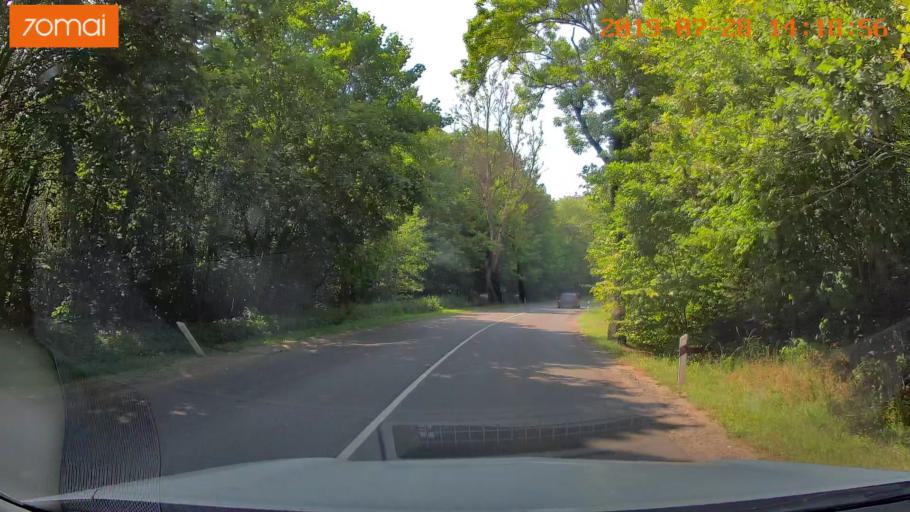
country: RU
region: Kaliningrad
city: Volochayevskoye
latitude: 54.8177
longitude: 20.2331
